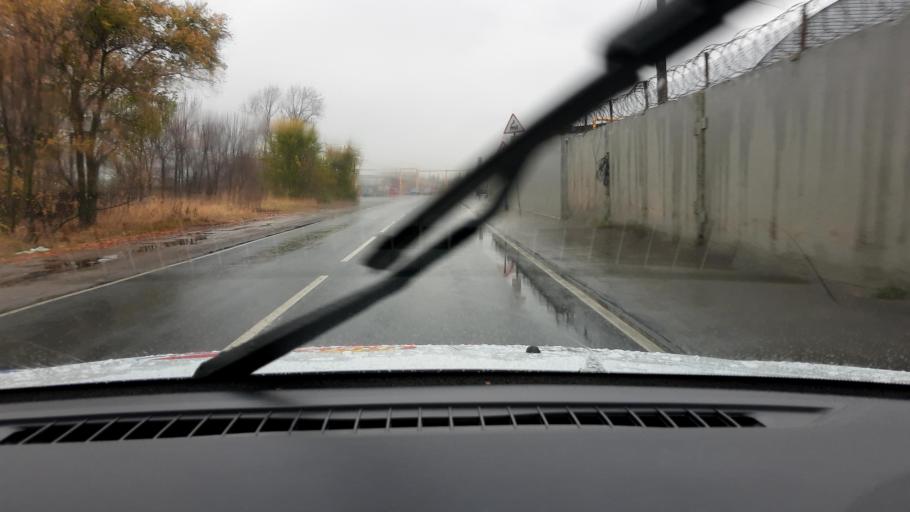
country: RU
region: Nizjnij Novgorod
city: Babino
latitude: 56.2568
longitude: 43.5942
